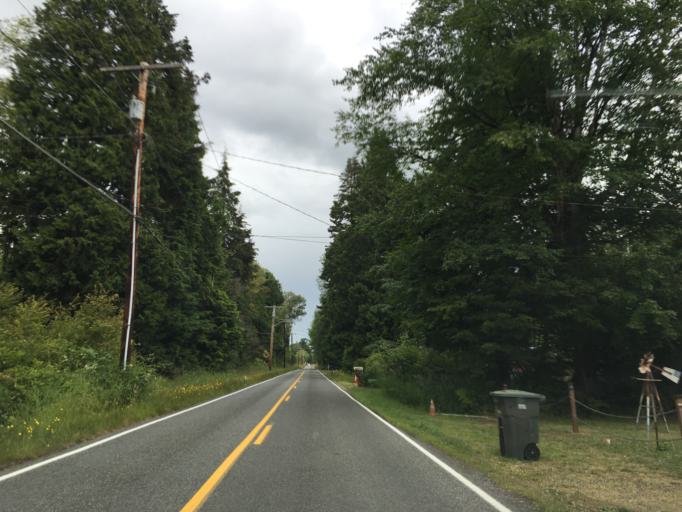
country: US
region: Washington
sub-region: Whatcom County
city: Birch Bay
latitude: 48.9433
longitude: -122.7553
